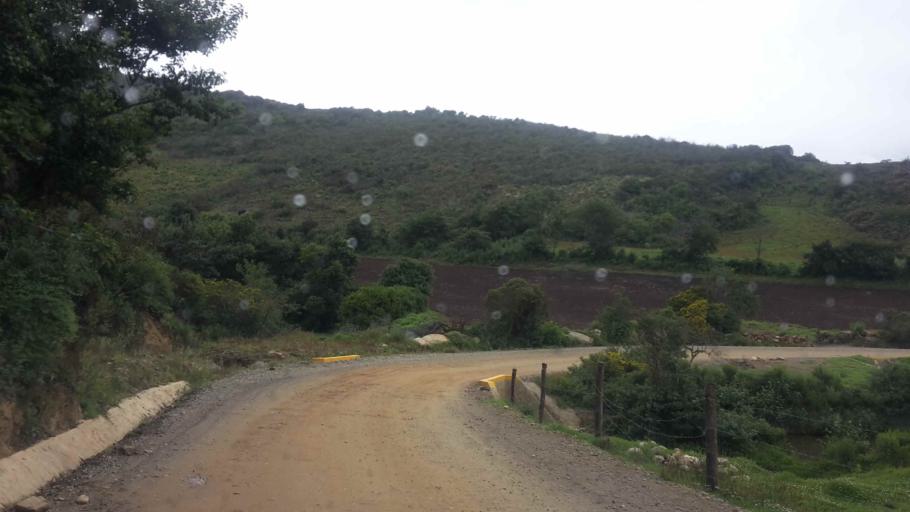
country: BO
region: Cochabamba
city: Totora
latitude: -17.5841
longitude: -65.2930
